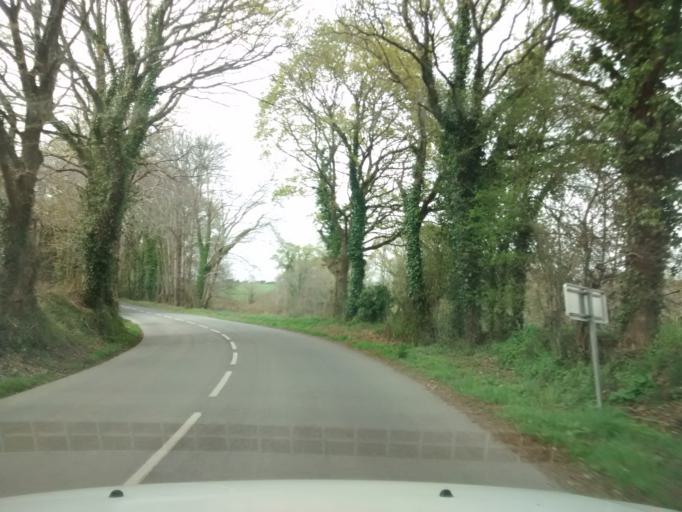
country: FR
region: Brittany
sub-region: Departement du Morbihan
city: Guidel-Plage
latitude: 47.7910
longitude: -3.5487
